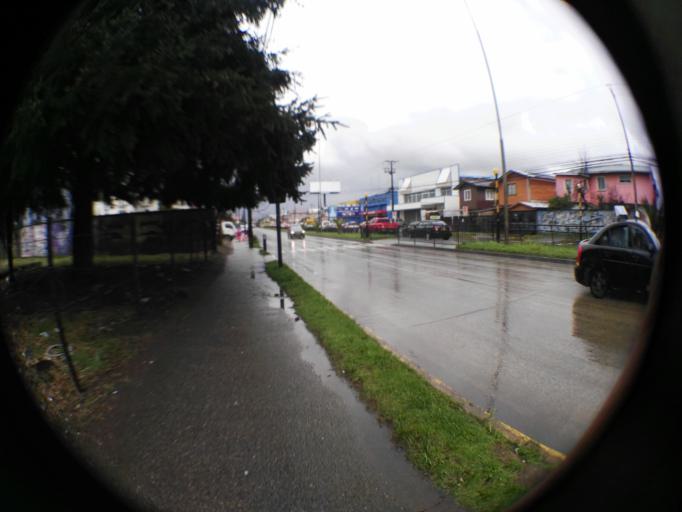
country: CL
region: Los Lagos
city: Las Animas
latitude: -39.8268
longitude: -73.2237
